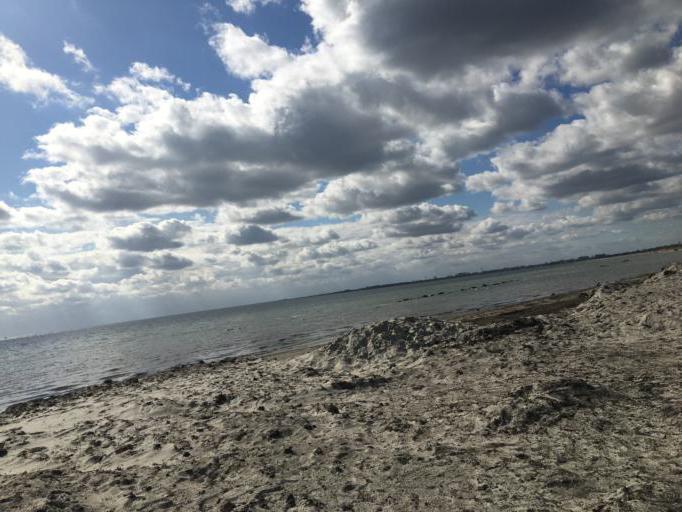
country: DK
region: Capital Region
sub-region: Brondby Kommune
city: Brondbyvester
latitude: 55.6118
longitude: 12.4383
